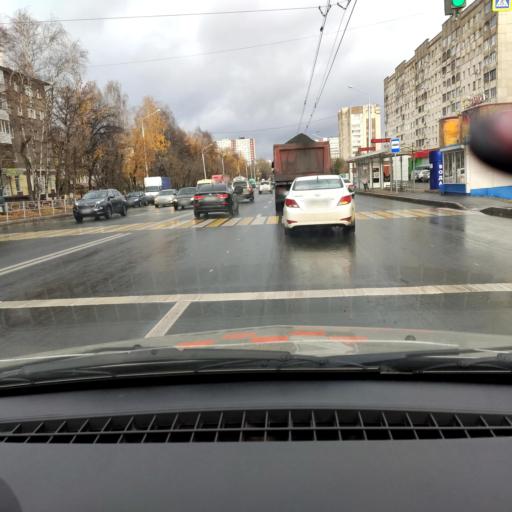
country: RU
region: Bashkortostan
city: Ufa
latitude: 54.7779
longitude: 56.0358
